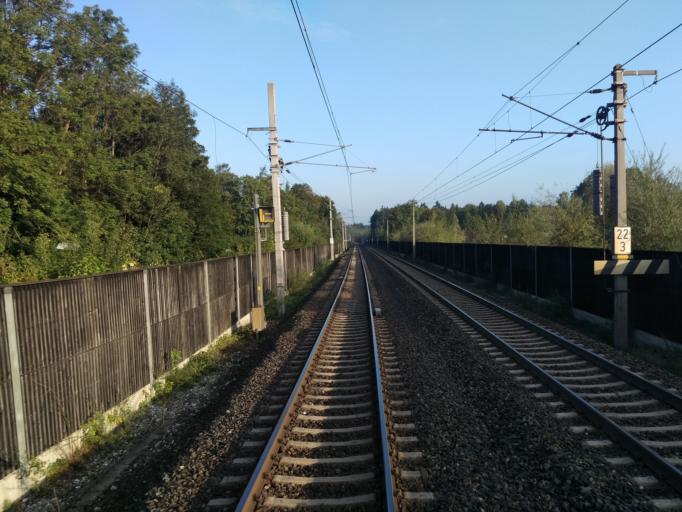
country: AT
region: Salzburg
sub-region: Politischer Bezirk Hallein
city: Kuchl
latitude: 47.6525
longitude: 13.1278
